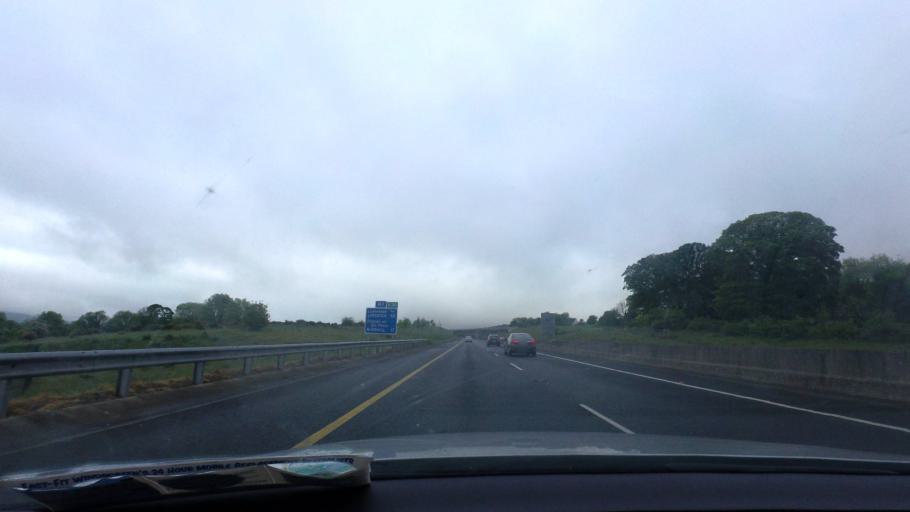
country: IE
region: Munster
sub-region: North Tipperary
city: Nenagh
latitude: 52.8434
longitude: -8.2671
